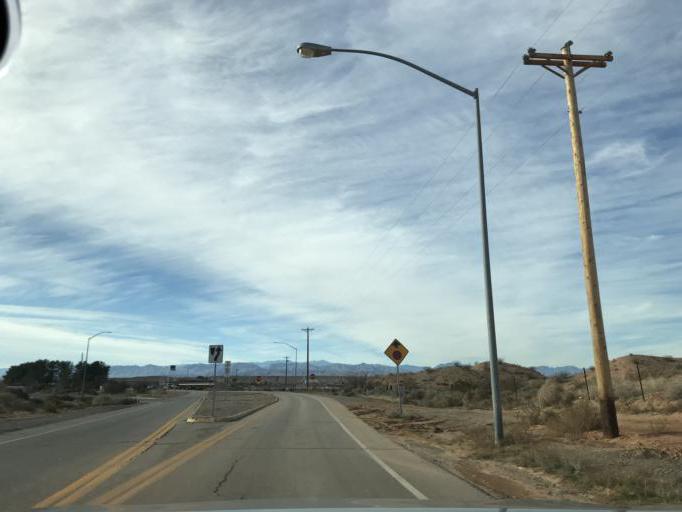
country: US
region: Nevada
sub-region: Clark County
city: Moapa Town
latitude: 36.6664
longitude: -114.5641
